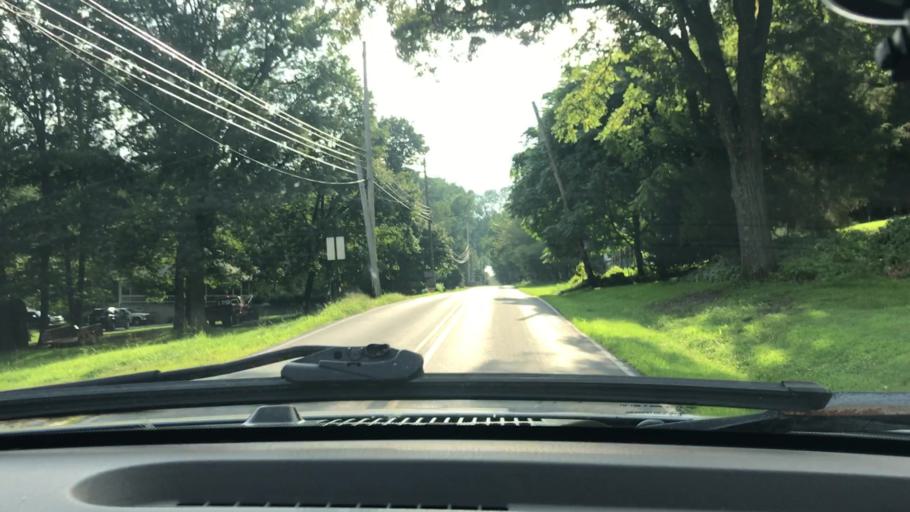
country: US
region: Pennsylvania
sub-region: Dauphin County
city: Hershey
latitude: 40.2210
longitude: -76.6394
